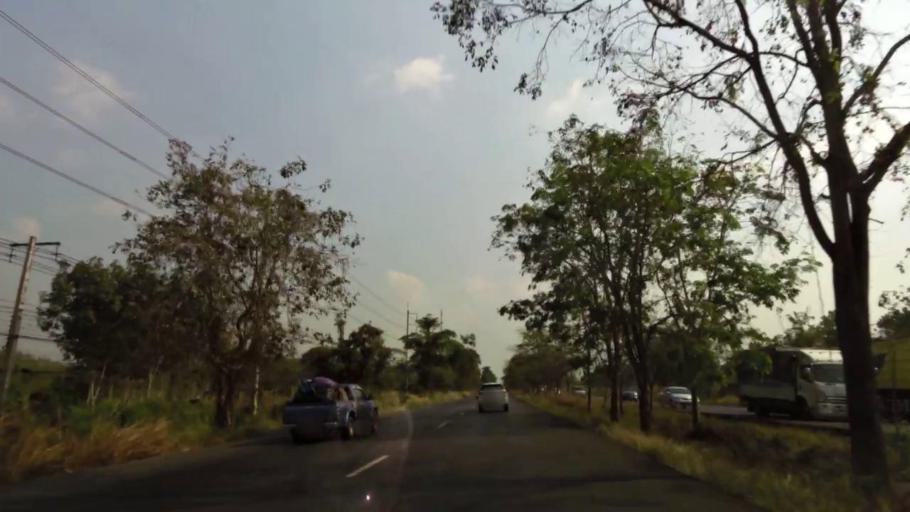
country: TH
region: Rayong
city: Wang Chan
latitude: 12.9518
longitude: 101.5115
